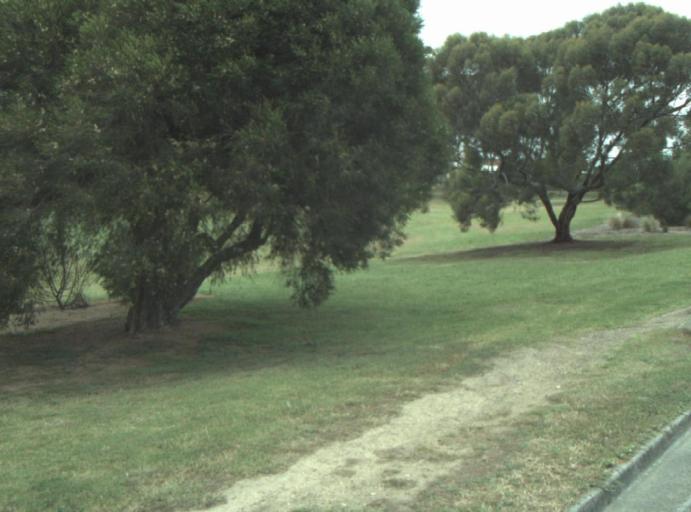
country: AU
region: Victoria
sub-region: Greater Geelong
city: Wandana Heights
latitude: -38.1734
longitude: 144.3072
